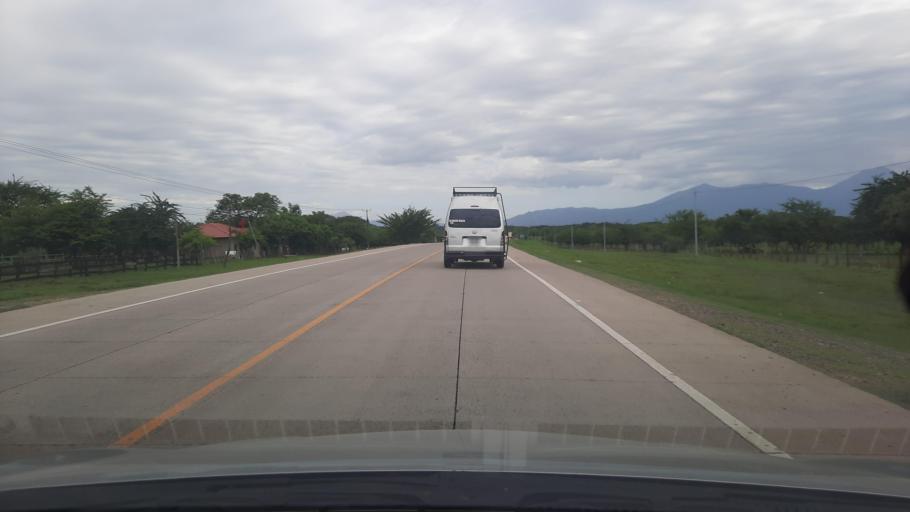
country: NI
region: Chinandega
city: Somotillo
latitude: 12.8839
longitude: -86.8503
